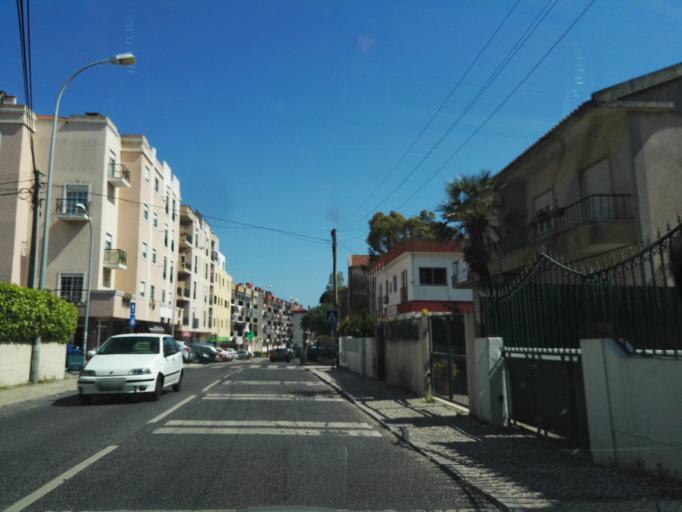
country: PT
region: Lisbon
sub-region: Sintra
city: Rio de Mouro
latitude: 38.7954
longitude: -9.3483
